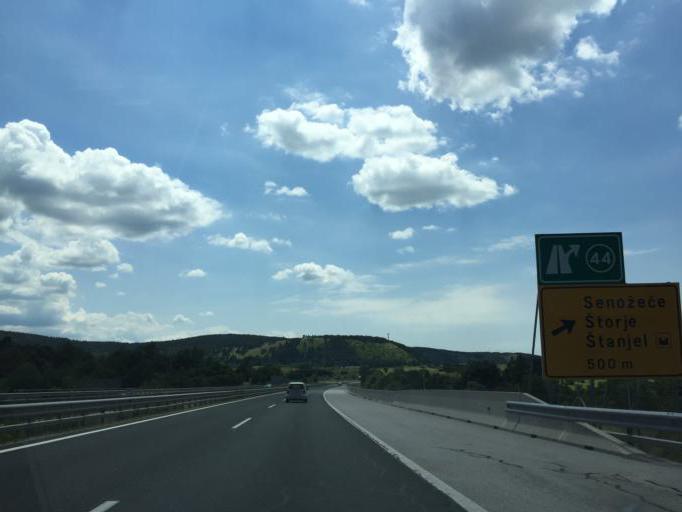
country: SI
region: Divaca
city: Divaca
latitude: 45.7284
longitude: 14.0171
